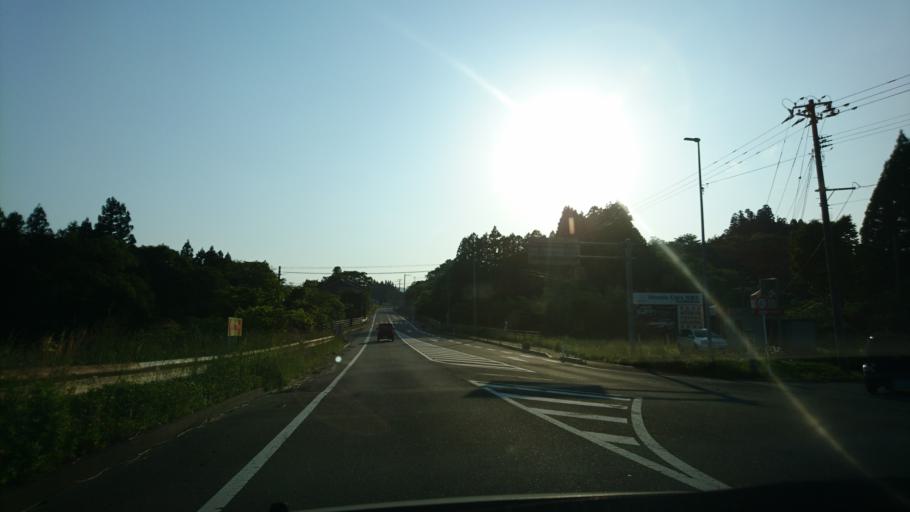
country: JP
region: Iwate
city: Ofunato
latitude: 38.9166
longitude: 141.5037
